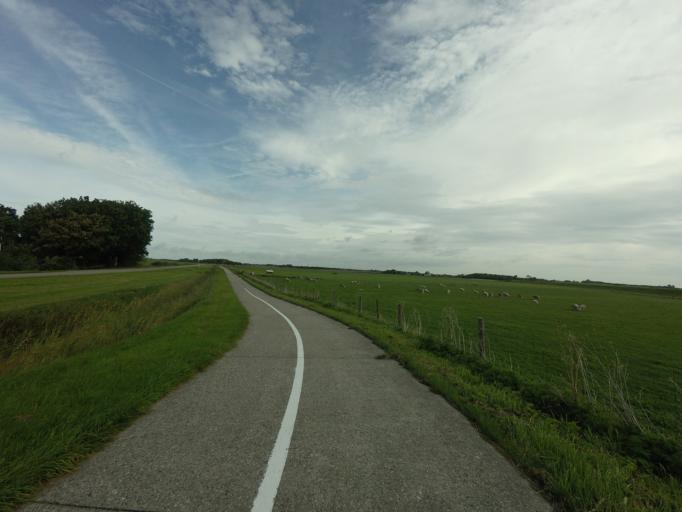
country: NL
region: North Holland
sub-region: Gemeente Texel
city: Den Burg
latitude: 53.0291
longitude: 4.7827
